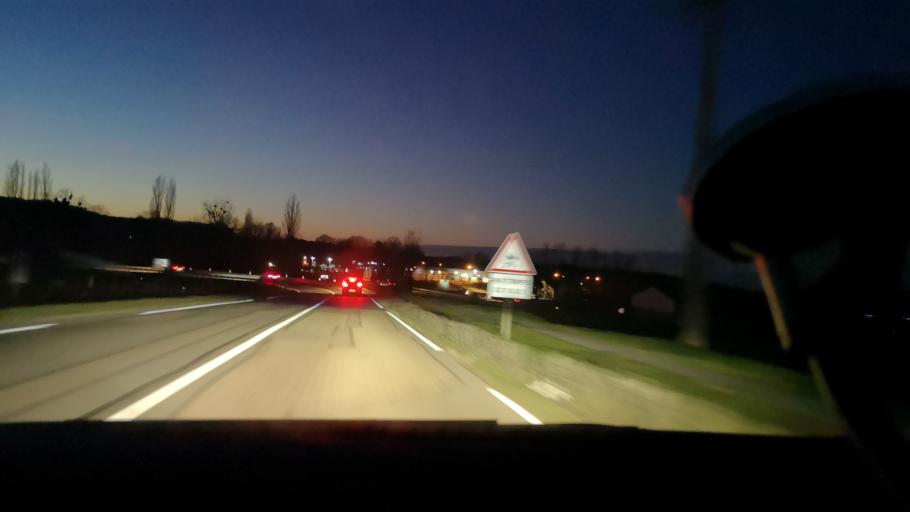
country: FR
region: Franche-Comte
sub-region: Departement du Jura
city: Poligny
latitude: 46.8359
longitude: 5.6933
